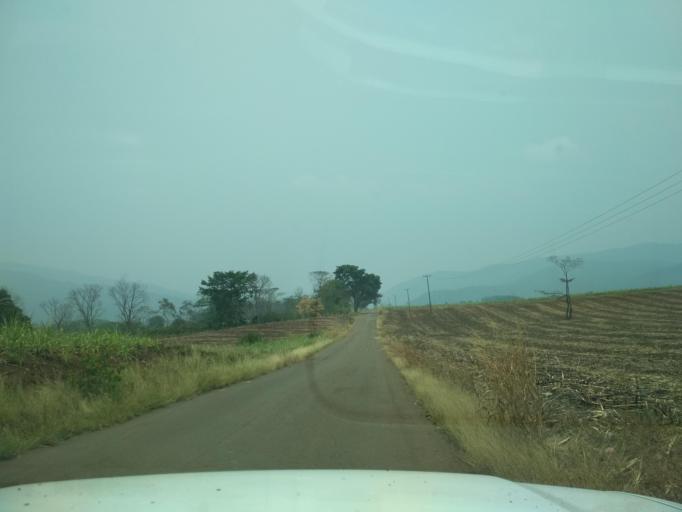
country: MX
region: Veracruz
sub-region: Tezonapa
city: Laguna Chica (Pueblo Nuevo)
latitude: 18.5199
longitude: -96.7525
